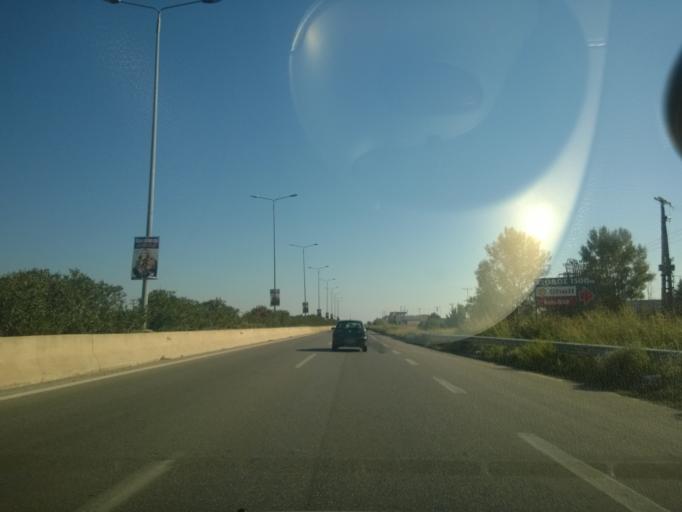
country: GR
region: Central Macedonia
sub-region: Nomos Chalkidikis
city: Lakkoma
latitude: 40.3940
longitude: 23.0339
